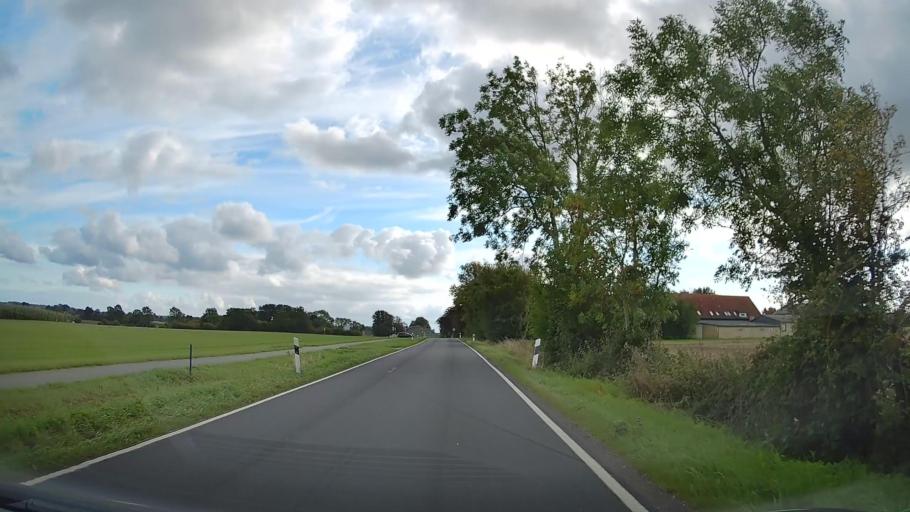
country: DE
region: Schleswig-Holstein
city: Steinberg
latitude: 54.7598
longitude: 9.7995
